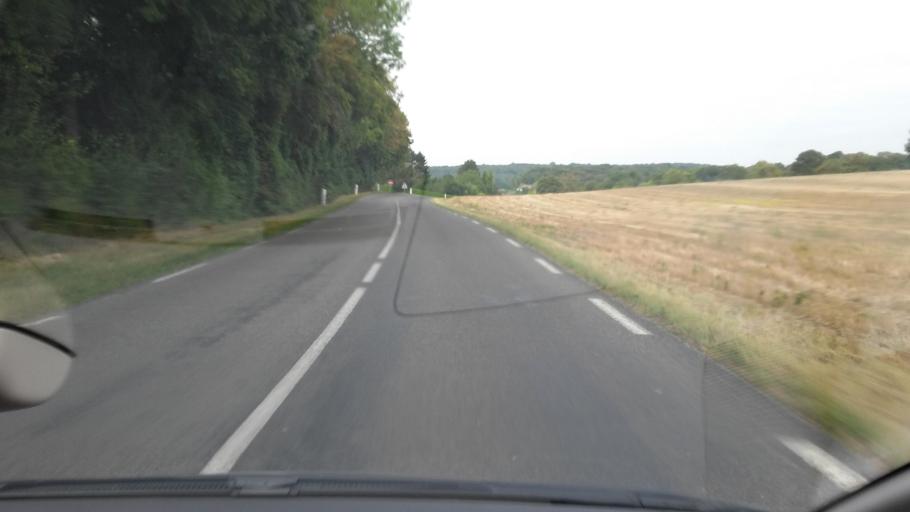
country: FR
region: Champagne-Ardenne
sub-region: Departement de la Marne
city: Verzenay
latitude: 49.1170
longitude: 4.1089
